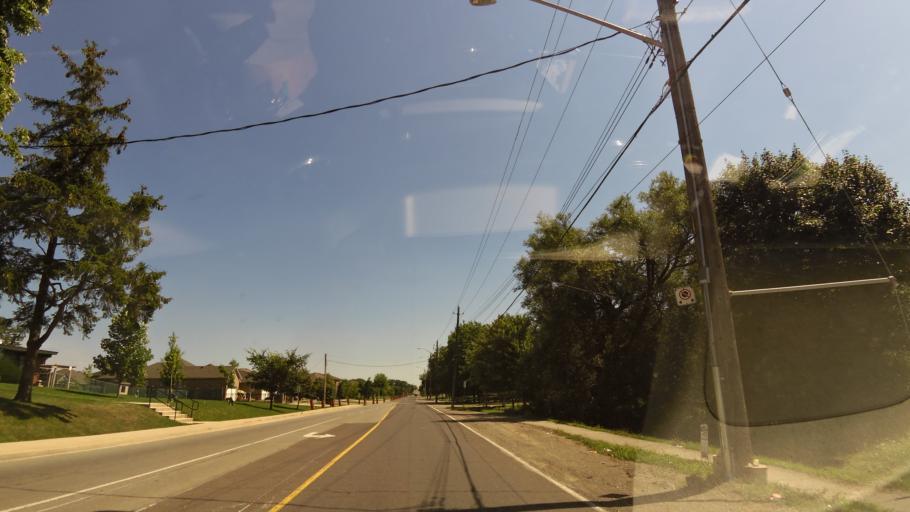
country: CA
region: Ontario
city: Ancaster
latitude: 43.2094
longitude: -79.9224
